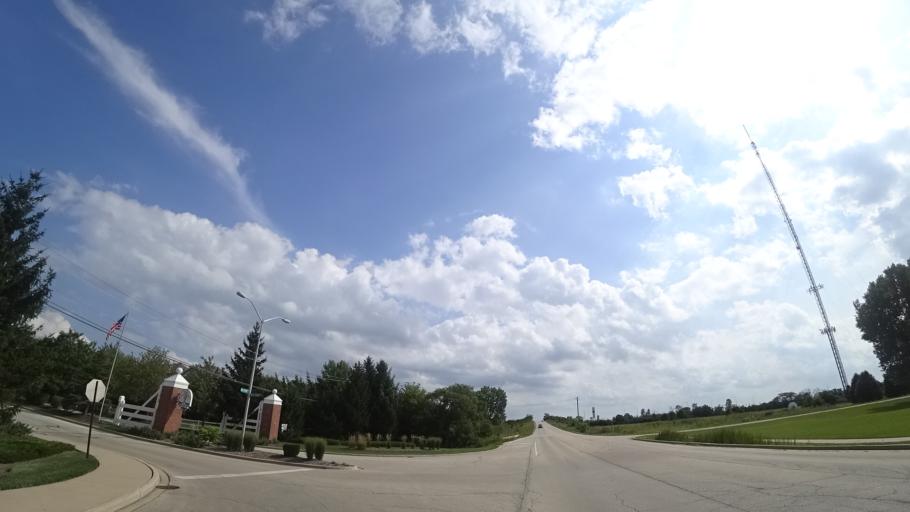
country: US
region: Illinois
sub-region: Cook County
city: Tinley Park
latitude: 41.5544
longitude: -87.7835
